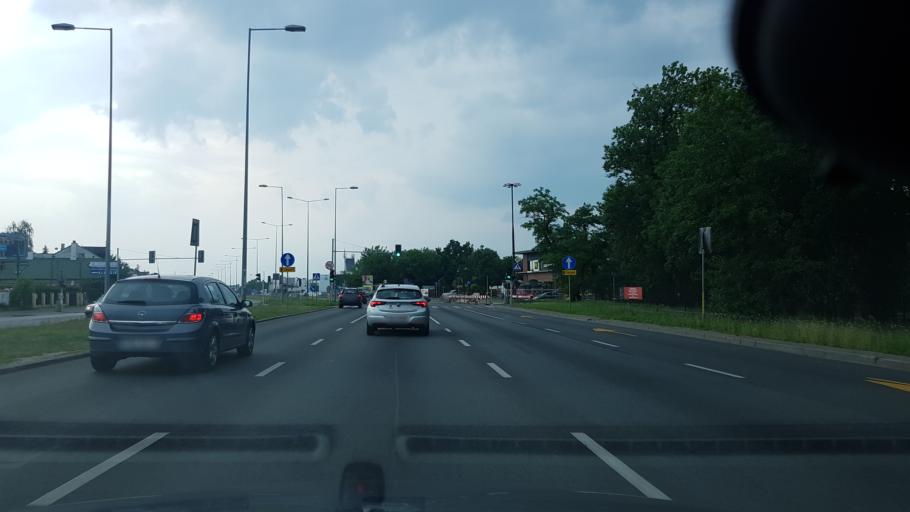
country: PL
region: Masovian Voivodeship
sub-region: Warszawa
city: Bialoleka
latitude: 52.3305
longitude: 20.9664
